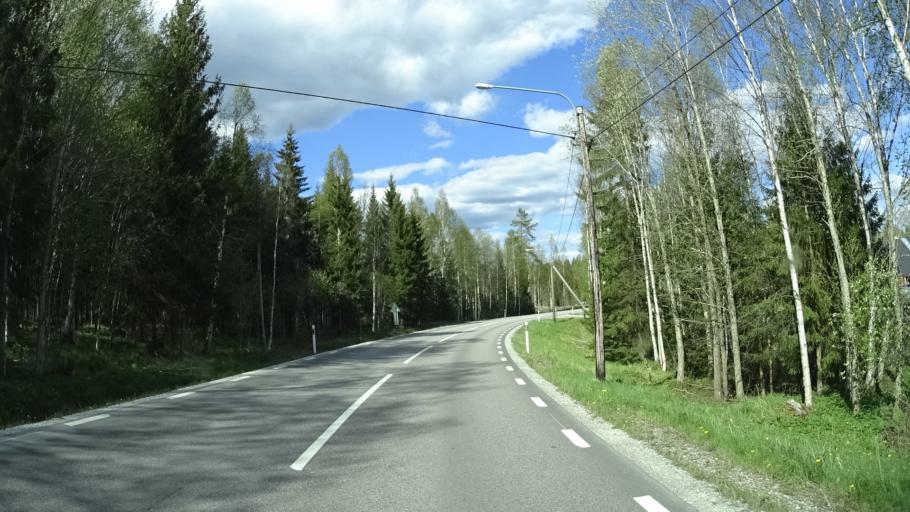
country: SE
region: OErebro
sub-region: Nora Kommun
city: As
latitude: 59.4559
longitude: 14.8336
